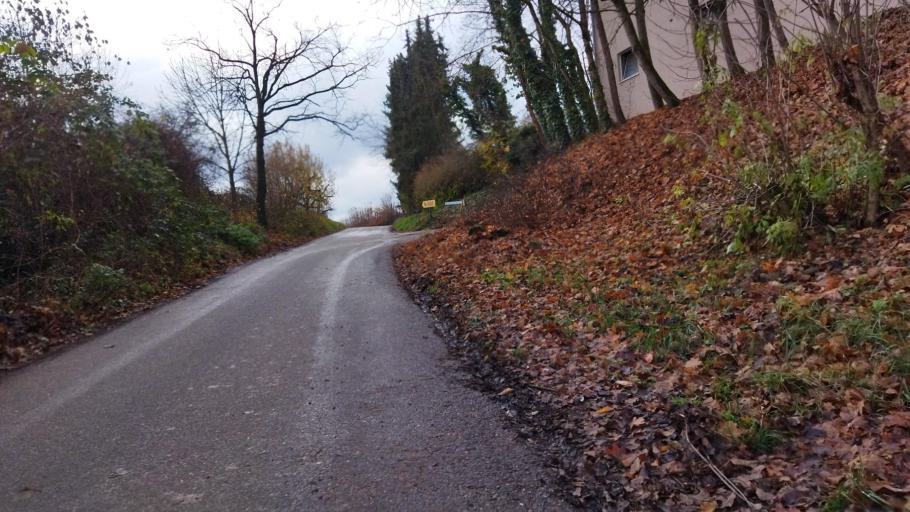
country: DE
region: Baden-Wuerttemberg
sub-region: Regierungsbezirk Stuttgart
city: Erligheim
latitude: 49.0181
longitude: 9.0879
